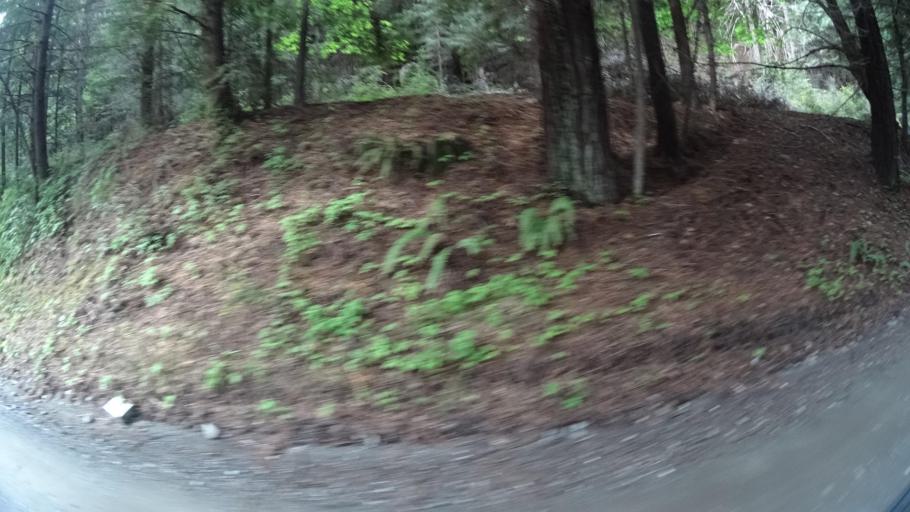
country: US
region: California
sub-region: Humboldt County
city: Redway
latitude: 40.3249
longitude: -123.8382
